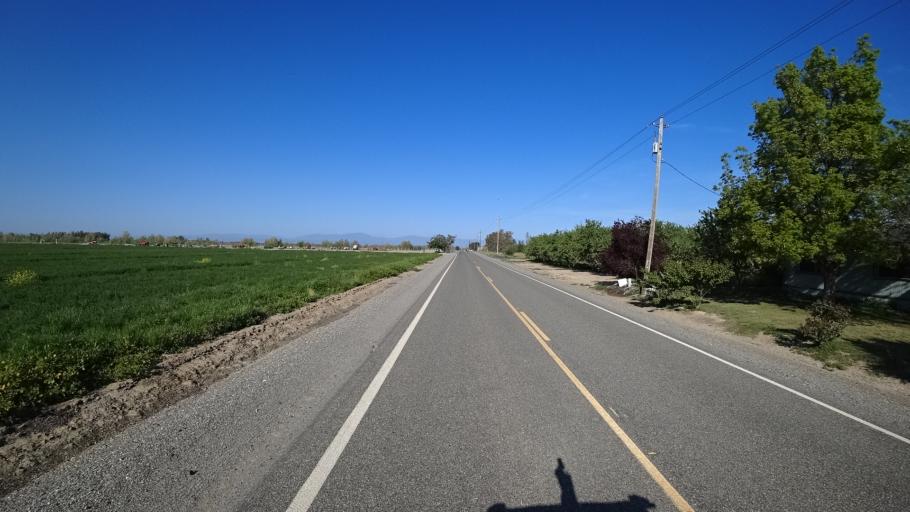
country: US
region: California
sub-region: Glenn County
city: Willows
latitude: 39.5533
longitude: -122.1571
